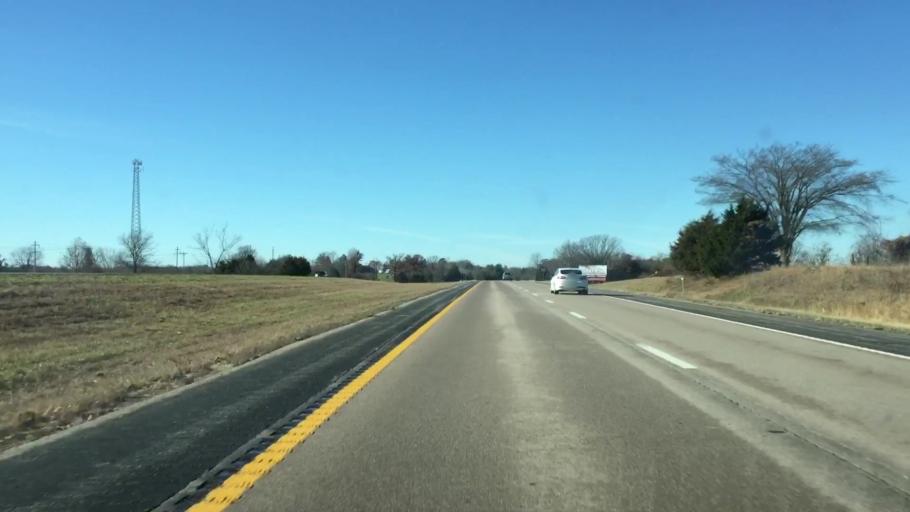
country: US
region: Missouri
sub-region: Miller County
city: Eldon
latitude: 38.3726
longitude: -92.4546
